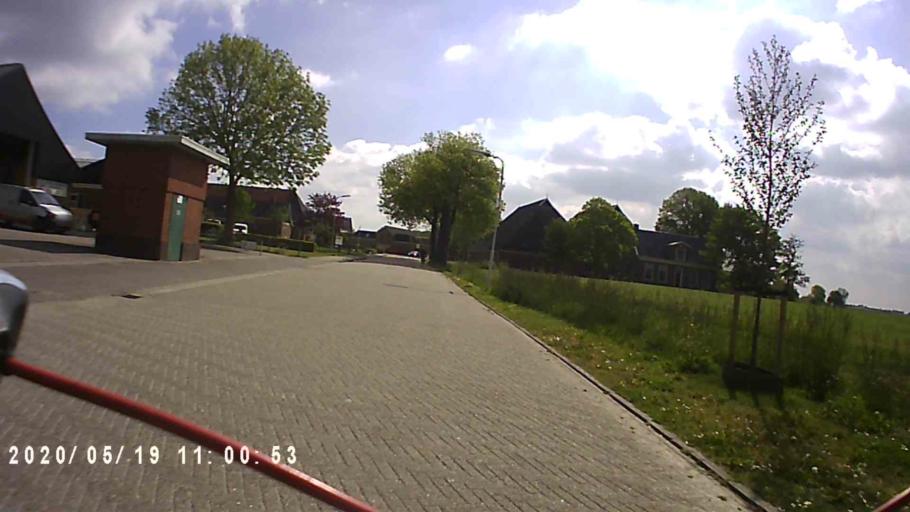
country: NL
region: Groningen
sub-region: Gemeente Zuidhorn
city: Grijpskerk
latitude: 53.3031
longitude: 6.2703
